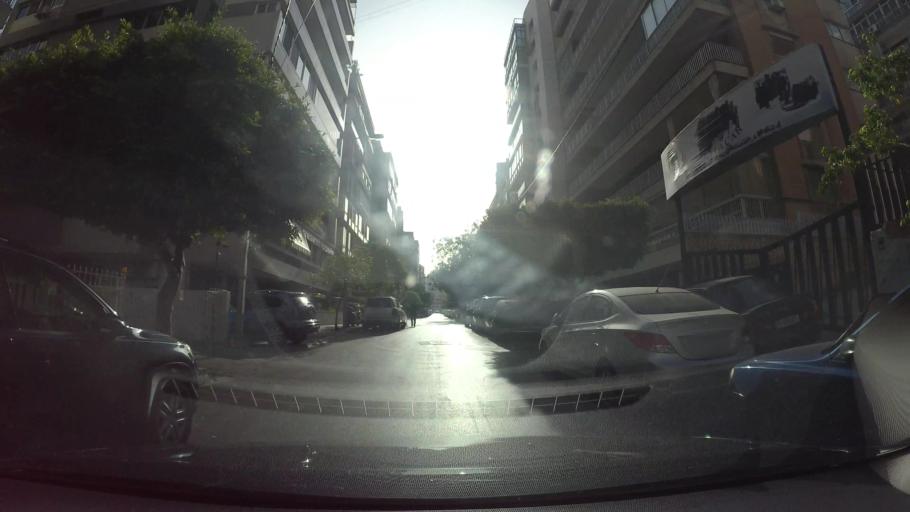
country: LB
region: Beyrouth
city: Ra's Bayrut
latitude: 33.8890
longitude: 35.4789
